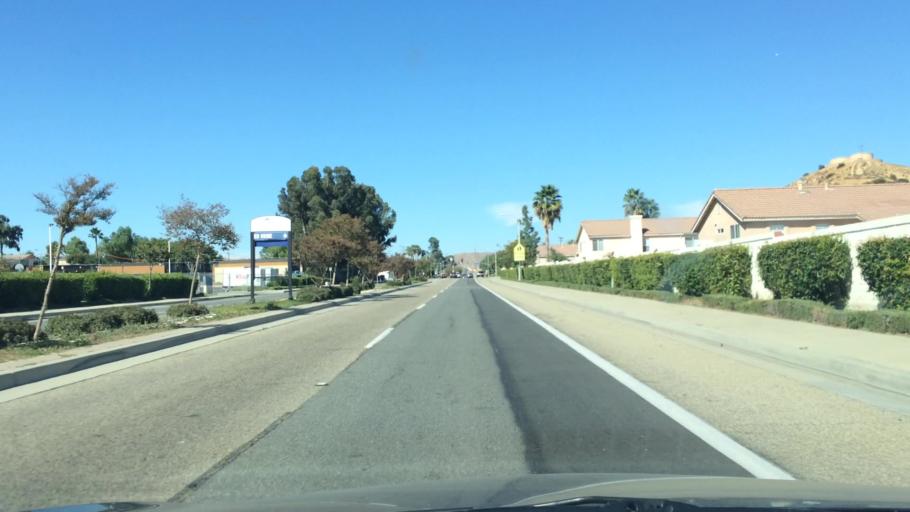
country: US
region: California
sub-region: Riverside County
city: Lake Elsinore
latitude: 33.6922
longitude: -117.3901
